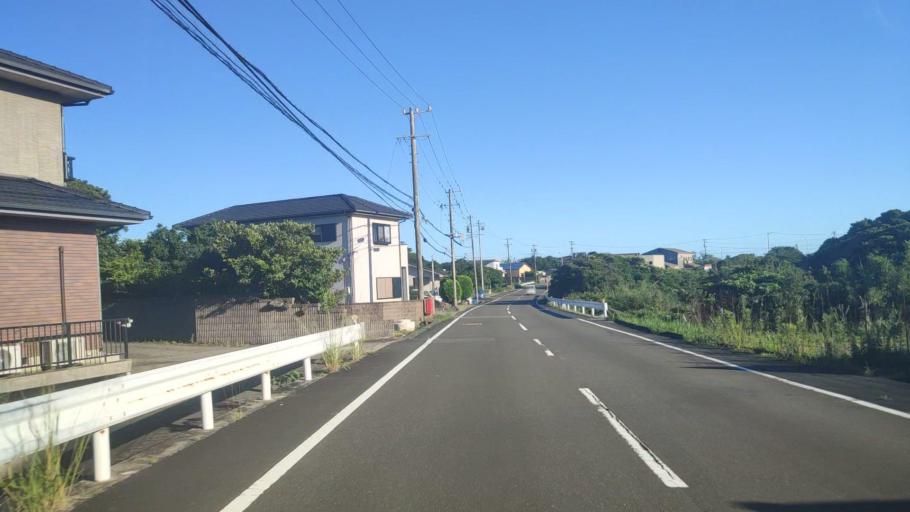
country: JP
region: Mie
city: Toba
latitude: 34.2889
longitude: 136.8919
